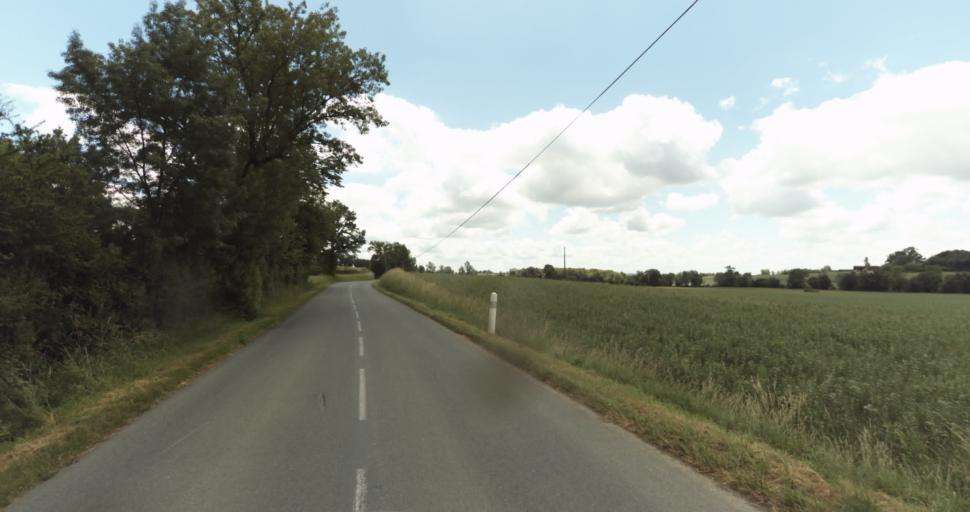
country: FR
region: Aquitaine
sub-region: Departement du Lot-et-Garonne
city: Villereal
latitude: 44.6880
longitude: 0.7540
